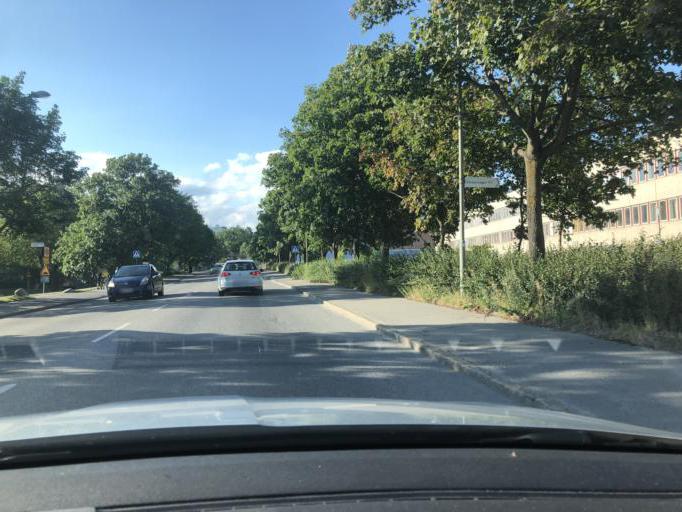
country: SE
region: Stockholm
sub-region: Huddinge Kommun
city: Segeltorp
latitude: 59.2746
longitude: 17.9036
